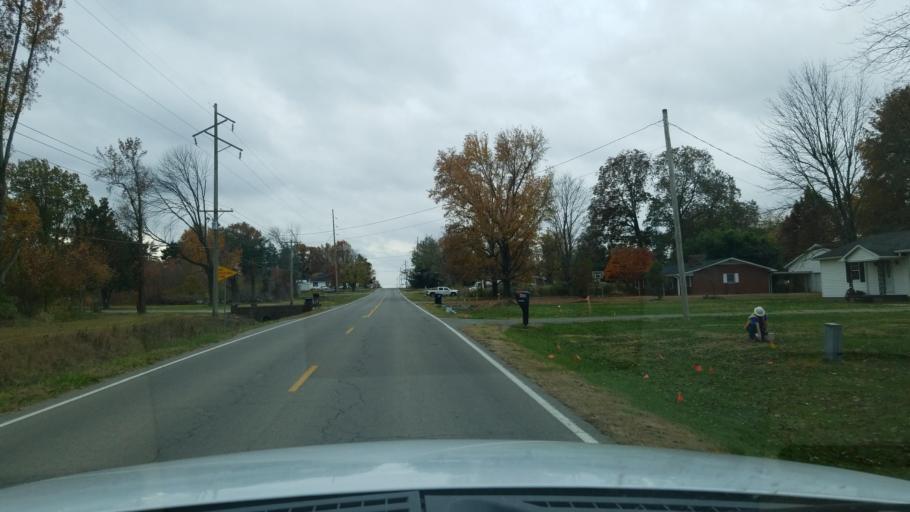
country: US
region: Illinois
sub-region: Saline County
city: Eldorado
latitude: 37.7994
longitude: -88.4383
